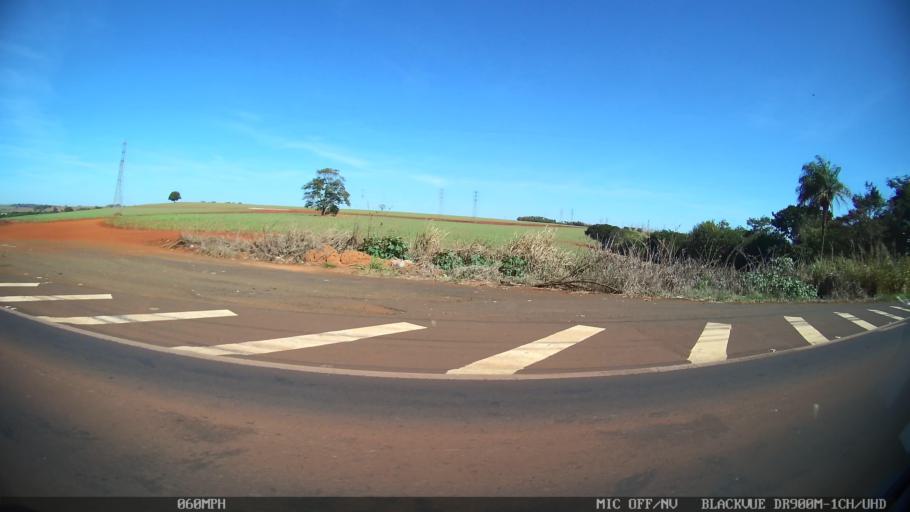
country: BR
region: Sao Paulo
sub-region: Sao Joaquim Da Barra
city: Sao Joaquim da Barra
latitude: -20.5257
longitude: -47.8384
